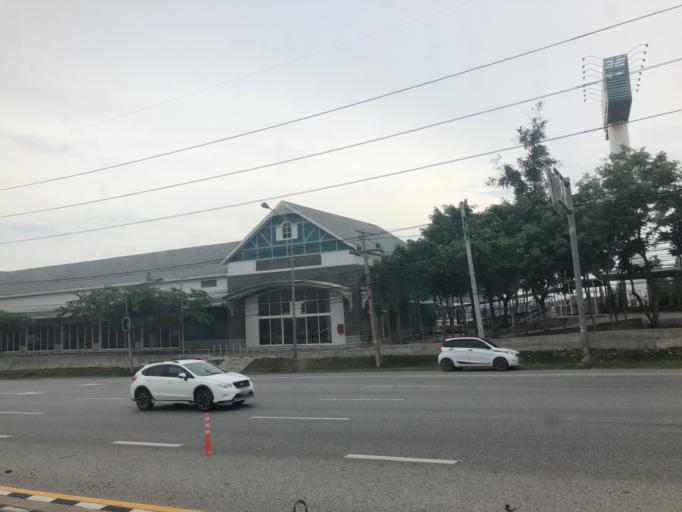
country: TH
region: Chon Buri
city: Bang Lamung
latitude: 13.0904
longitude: 100.9164
